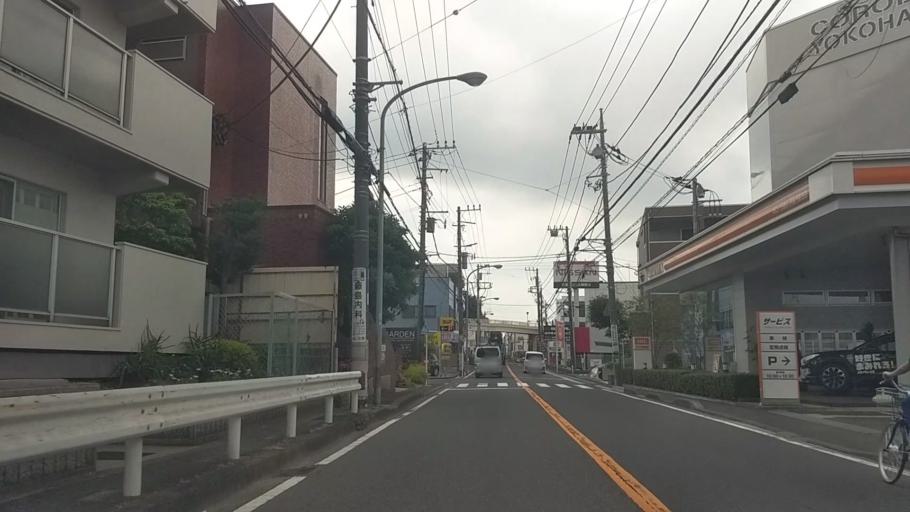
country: JP
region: Kanagawa
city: Kamakura
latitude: 35.3855
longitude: 139.5362
